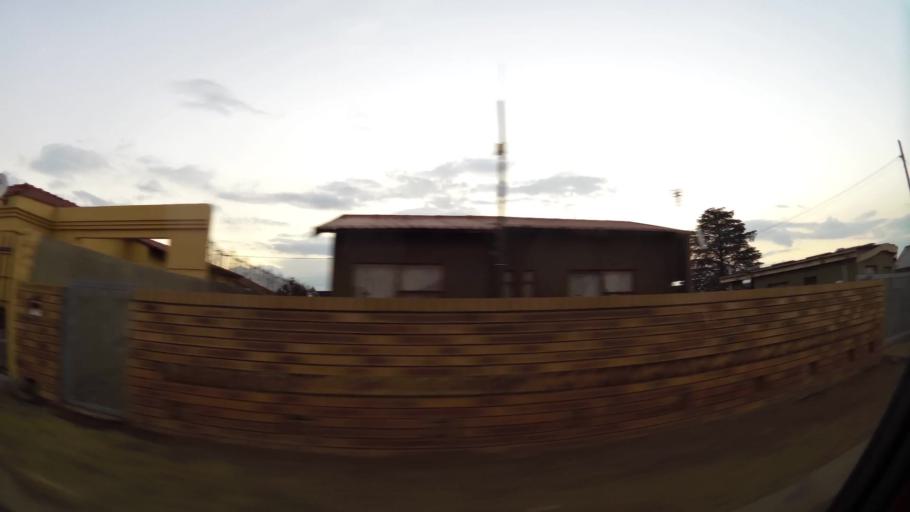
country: ZA
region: Gauteng
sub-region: City of Johannesburg Metropolitan Municipality
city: Orange Farm
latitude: -26.5484
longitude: 27.8490
